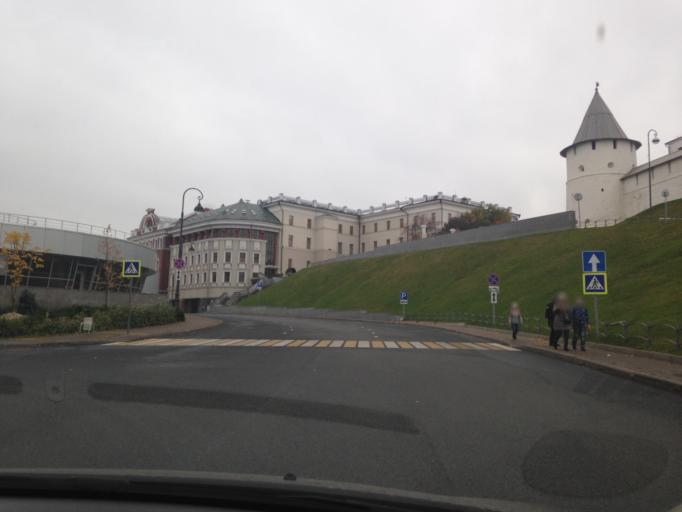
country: RU
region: Tatarstan
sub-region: Gorod Kazan'
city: Kazan
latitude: 55.7977
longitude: 49.1093
